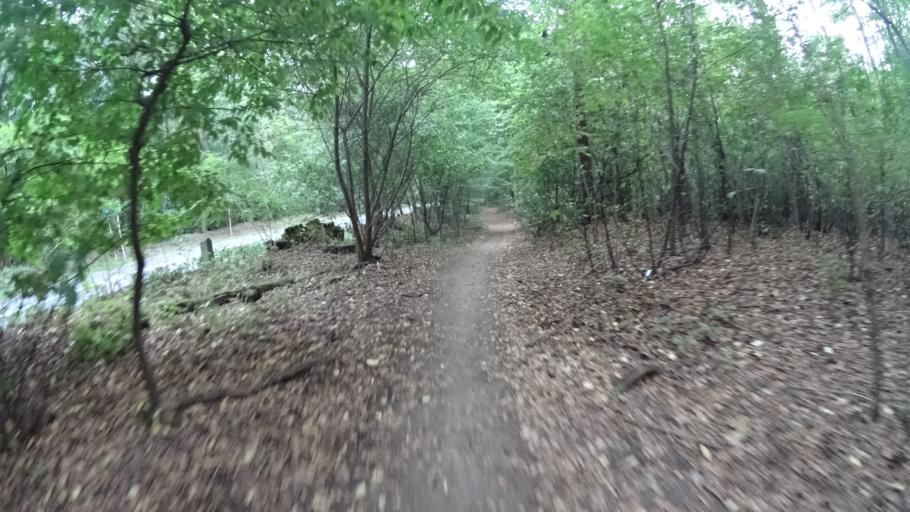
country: PL
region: Masovian Voivodeship
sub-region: Powiat pruszkowski
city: Granica
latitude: 52.1298
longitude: 20.7997
